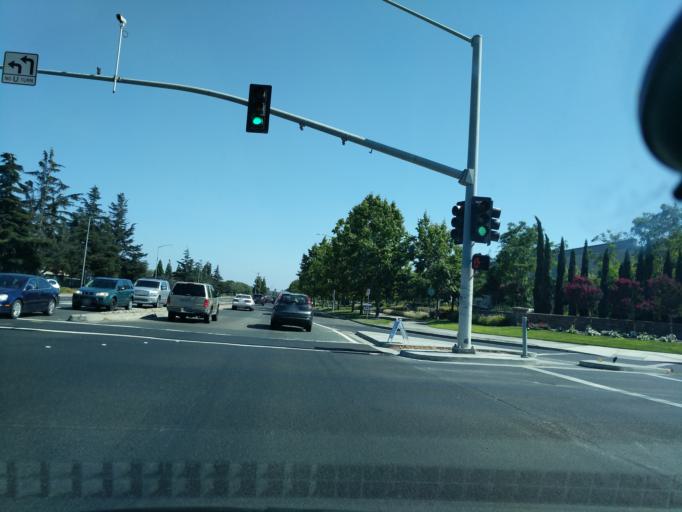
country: US
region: California
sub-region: Alameda County
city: Hayward
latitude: 37.6172
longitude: -122.0885
